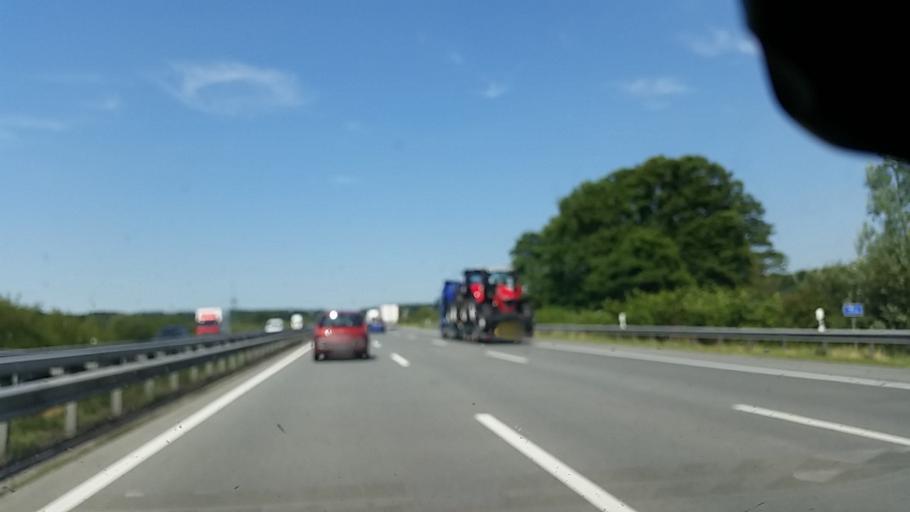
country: DE
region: Lower Saxony
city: Reessum
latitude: 53.1450
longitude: 9.2260
